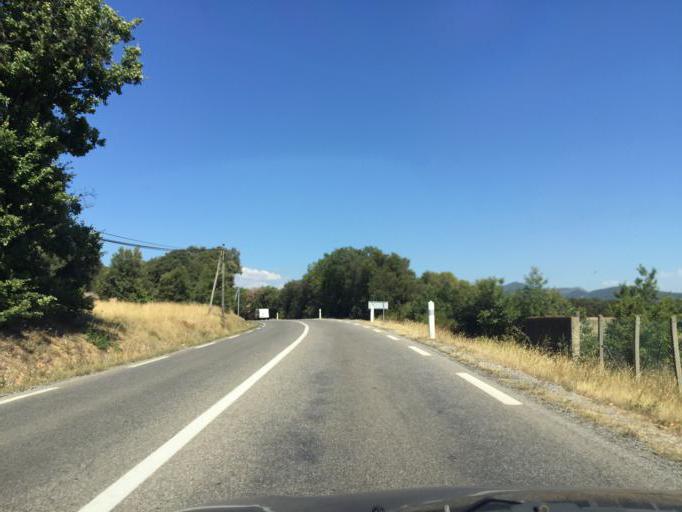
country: FR
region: Provence-Alpes-Cote d'Azur
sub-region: Departement des Alpes-de-Haute-Provence
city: Les Mees
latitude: 44.0471
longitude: 5.9595
